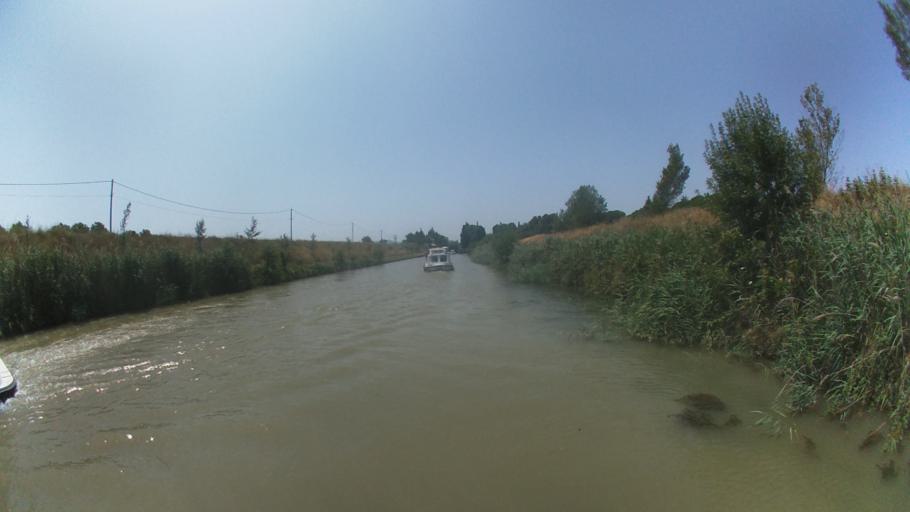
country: FR
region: Languedoc-Roussillon
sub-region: Departement de l'Aude
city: Puicheric
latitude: 43.2322
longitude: 2.6412
